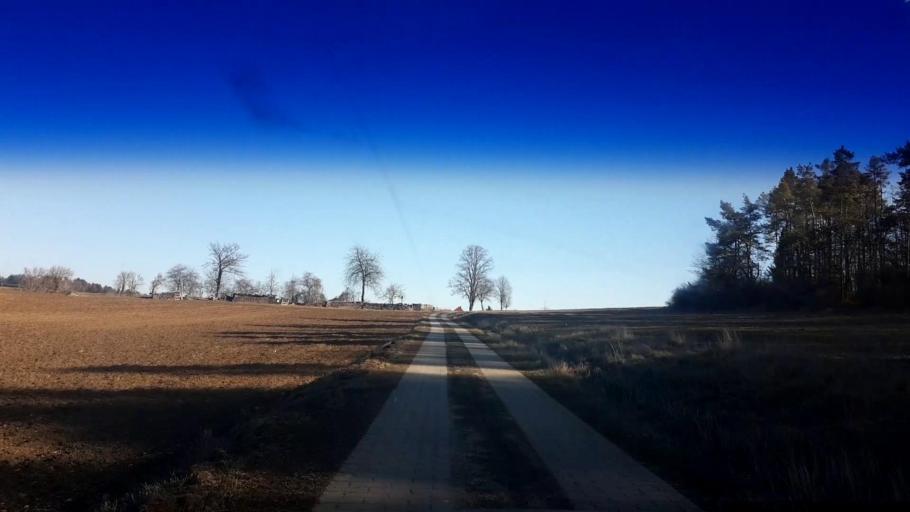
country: DE
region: Bavaria
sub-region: Upper Franconia
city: Poxdorf
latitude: 49.9657
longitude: 11.0948
